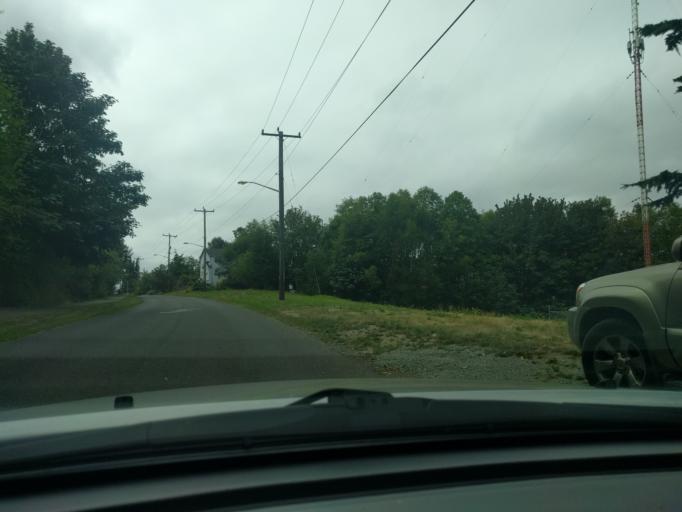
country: US
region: Washington
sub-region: King County
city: White Center
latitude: 47.5638
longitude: -122.3605
